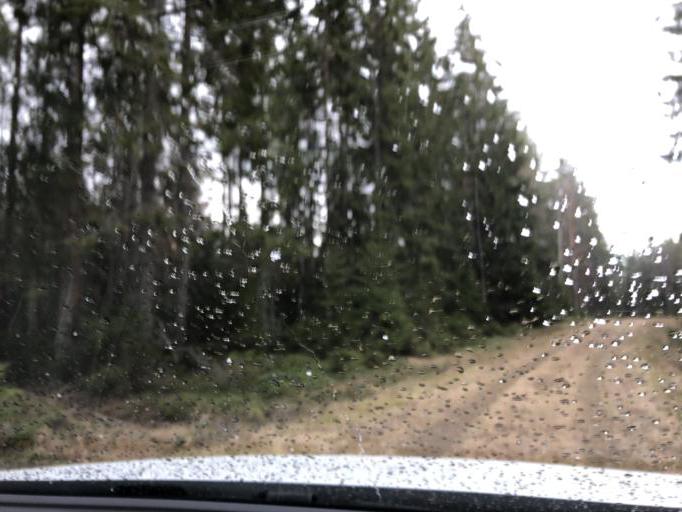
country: SE
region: Gaevleborg
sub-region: Gavle Kommun
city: Hedesunda
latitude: 60.3394
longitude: 17.0840
